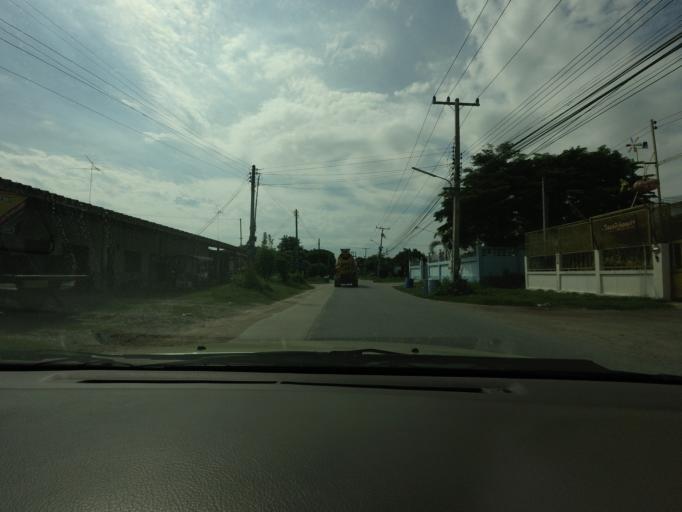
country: TH
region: Chon Buri
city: Chon Buri
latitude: 13.3233
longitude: 101.0018
